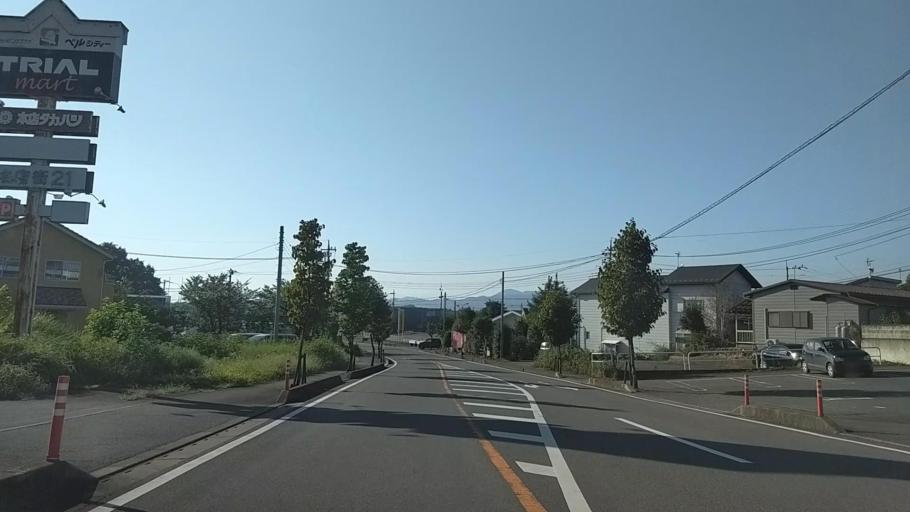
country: JP
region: Gunma
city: Annaka
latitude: 36.3189
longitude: 138.8762
